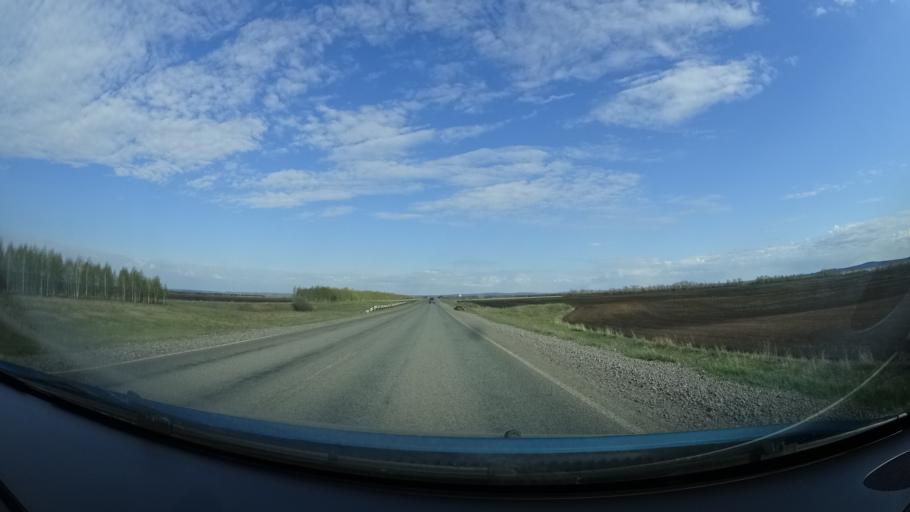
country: RU
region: Bashkortostan
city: Blagoveshchensk
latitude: 55.1966
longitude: 55.8323
